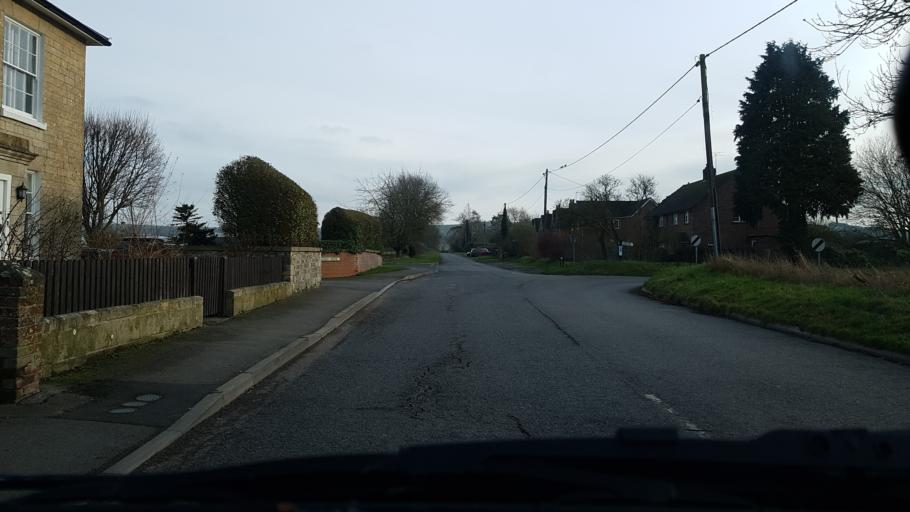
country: GB
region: England
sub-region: Wiltshire
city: Pewsey
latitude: 51.3345
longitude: -1.7668
